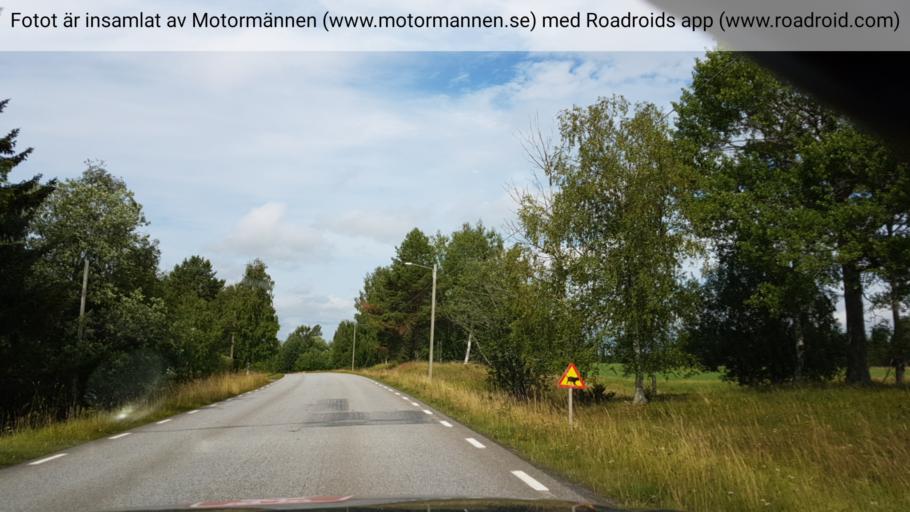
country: SE
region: Jaemtland
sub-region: Krokoms Kommun
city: Krokom
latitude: 63.2652
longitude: 14.3946
